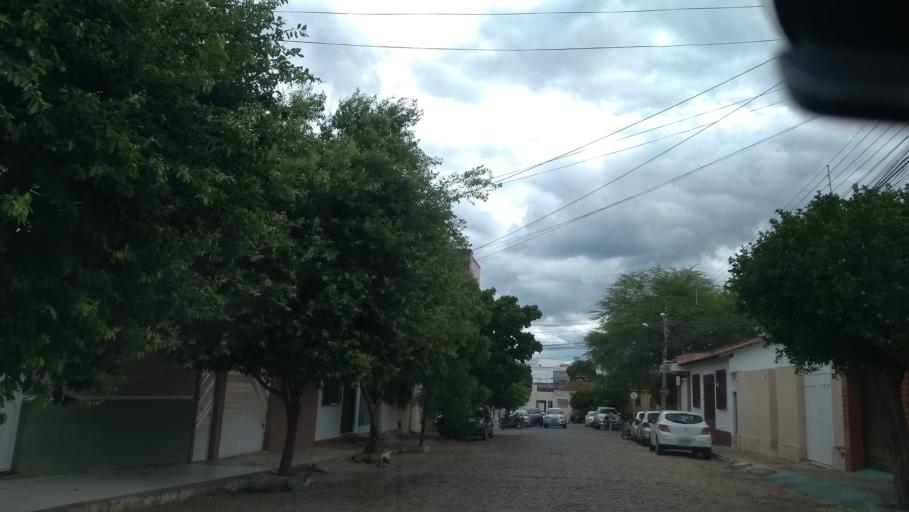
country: BR
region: Bahia
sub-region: Brumado
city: Brumado
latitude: -14.2072
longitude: -41.6680
